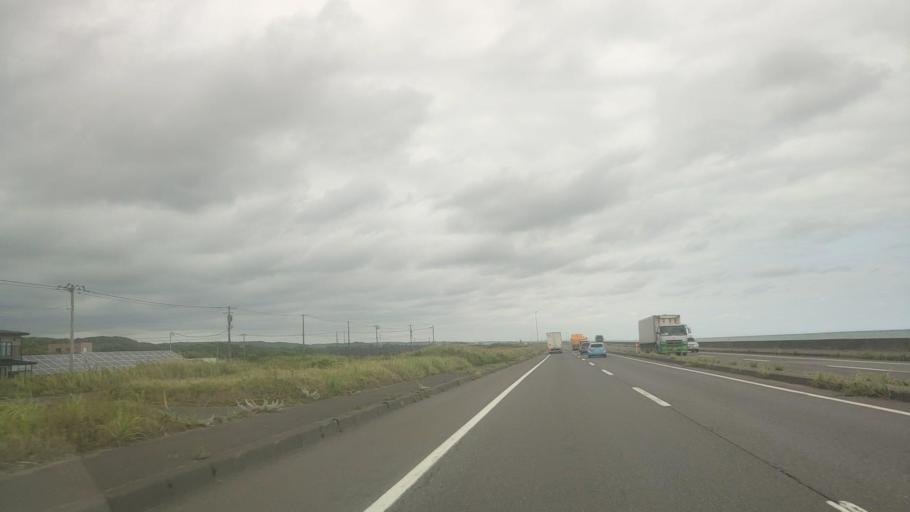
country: JP
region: Hokkaido
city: Shiraoi
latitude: 42.5542
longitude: 141.3726
